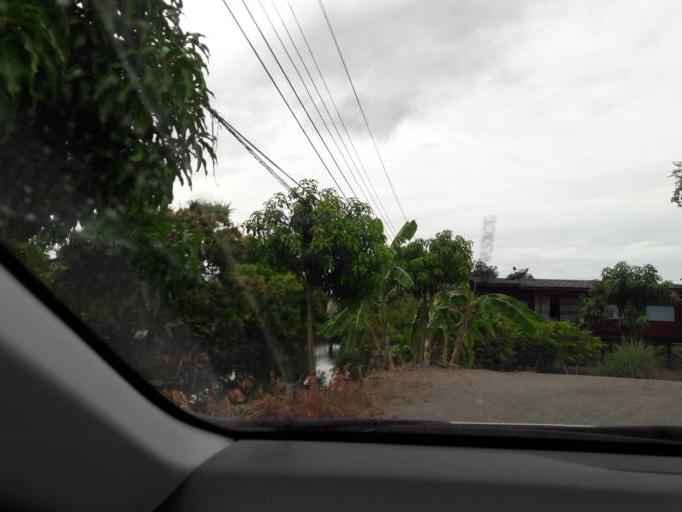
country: TH
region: Ratchaburi
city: Damnoen Saduak
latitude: 13.5452
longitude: 99.9786
